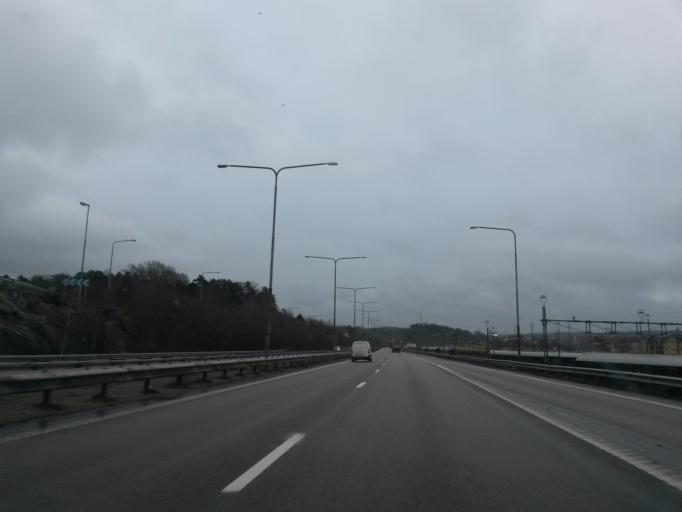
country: SE
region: Vaestra Goetaland
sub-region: Uddevalla Kommun
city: Uddevalla
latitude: 58.3556
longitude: 11.9162
